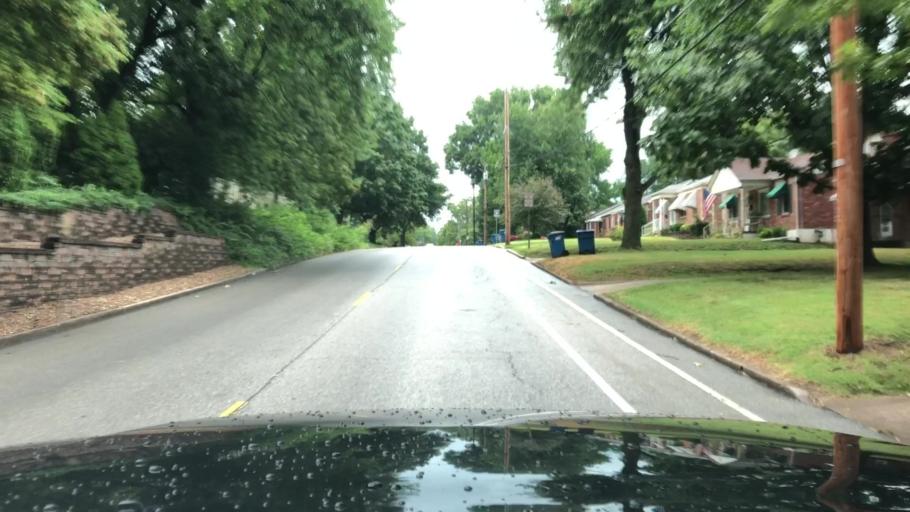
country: US
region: Missouri
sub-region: Saint Charles County
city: Saint Charles
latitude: 38.7930
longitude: -90.4996
